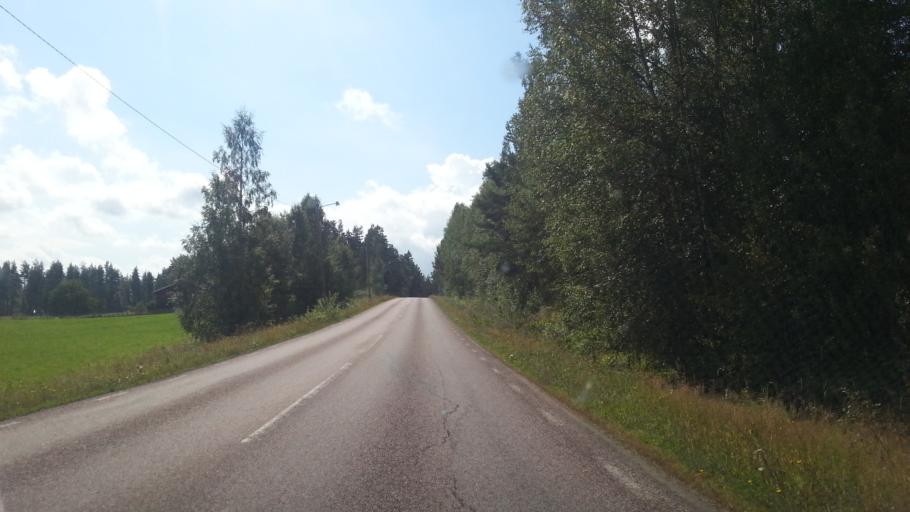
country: SE
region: Dalarna
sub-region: Faluns Kommun
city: Falun
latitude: 60.6202
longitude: 15.7666
